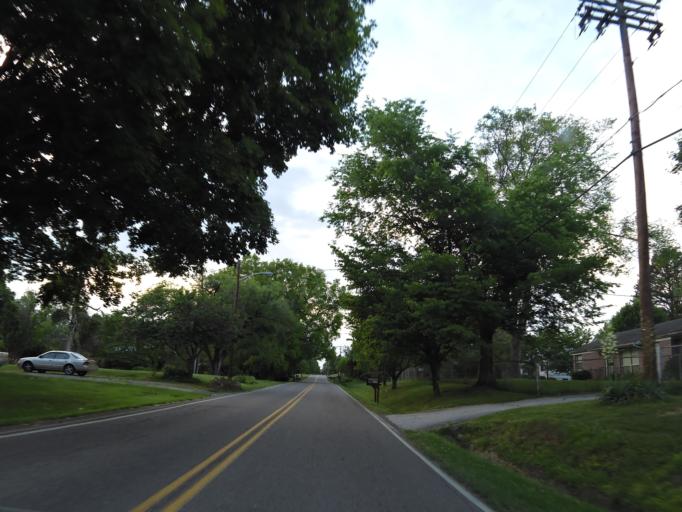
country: US
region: Tennessee
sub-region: Knox County
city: Knoxville
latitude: 36.0355
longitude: -83.9052
